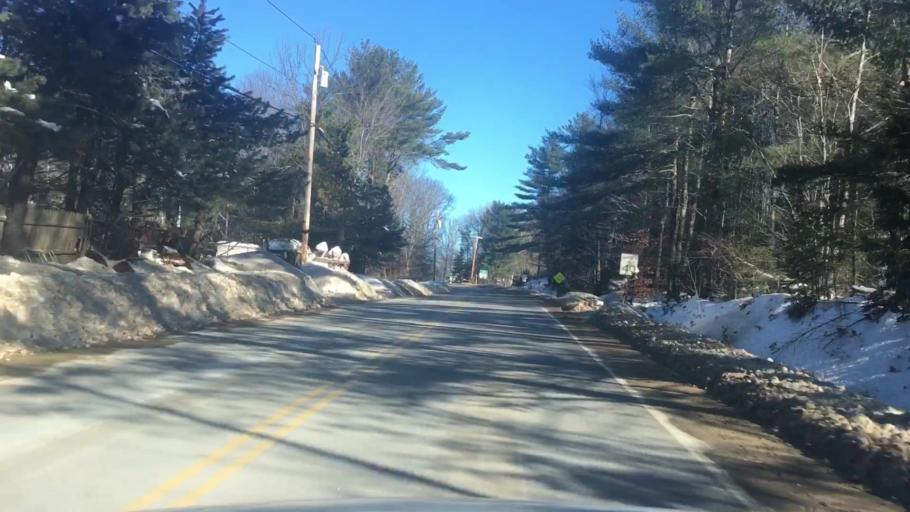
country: US
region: Maine
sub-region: Oxford County
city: Hartford
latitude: 44.3664
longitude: -70.3481
